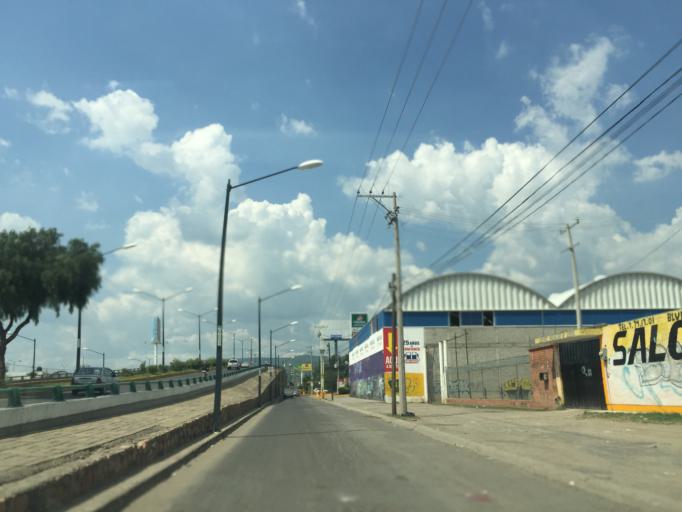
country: MX
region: Guanajuato
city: Leon
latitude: 21.1716
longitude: -101.6640
